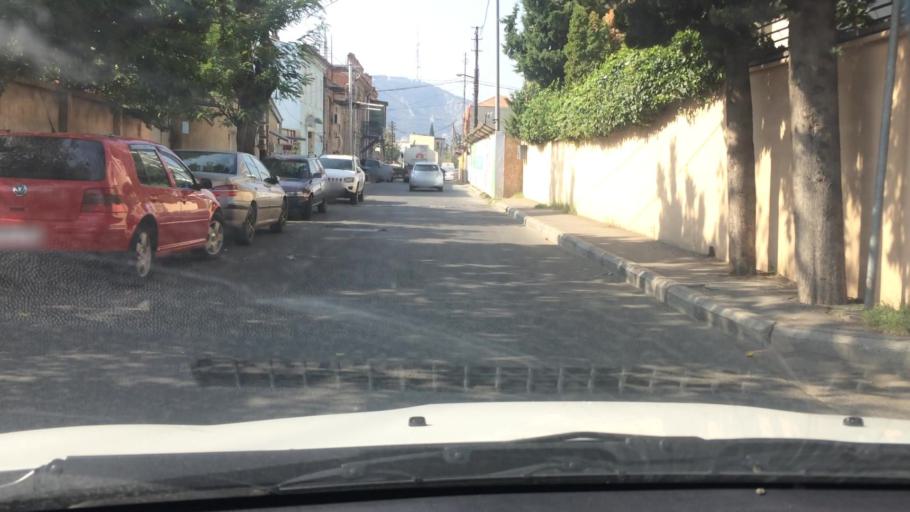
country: GE
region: T'bilisi
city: Tbilisi
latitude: 41.6909
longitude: 44.8258
